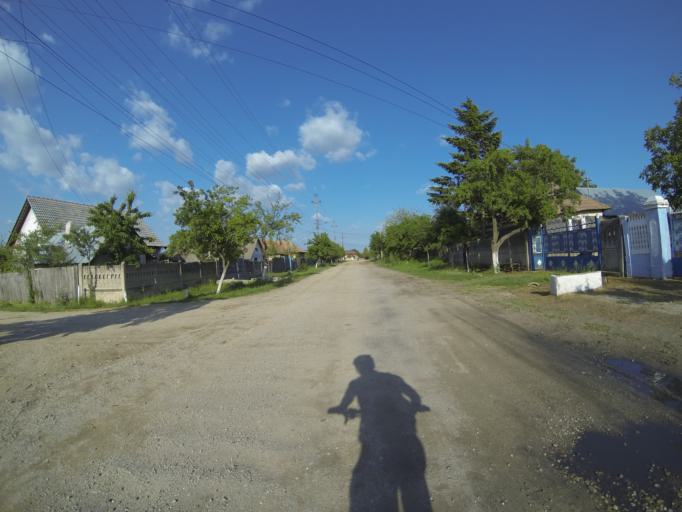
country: RO
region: Dolj
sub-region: Comuna Carpen
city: Carpen
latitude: 44.2919
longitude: 23.2451
